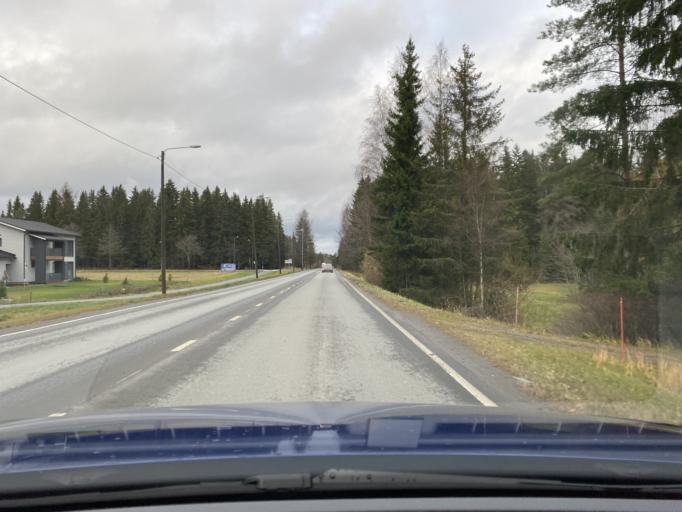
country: FI
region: Pirkanmaa
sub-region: Tampere
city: Lempaeaelae
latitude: 61.3405
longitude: 23.7541
